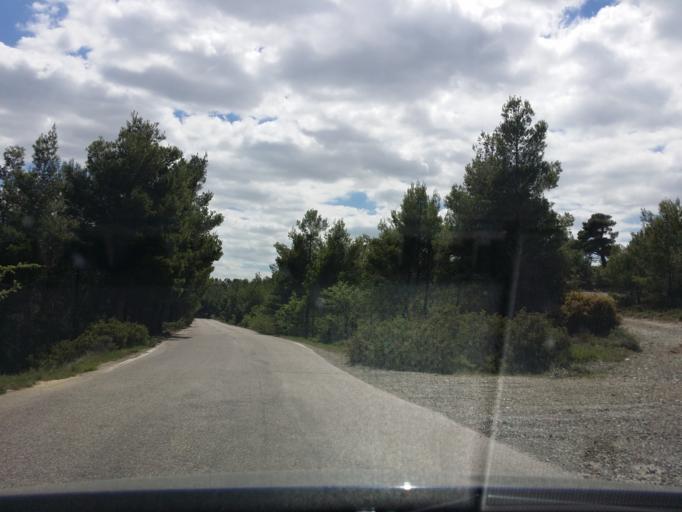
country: GR
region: Attica
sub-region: Nomarchia Dytikis Attikis
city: Fyli
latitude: 38.1265
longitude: 23.6473
